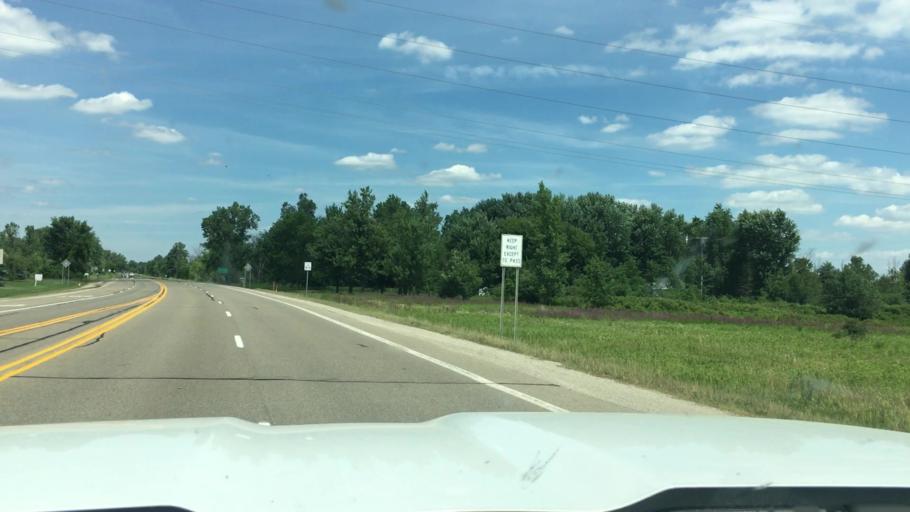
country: US
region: Michigan
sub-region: Lapeer County
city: Barnes Lake-Millers Lake
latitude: 43.2200
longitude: -83.3135
